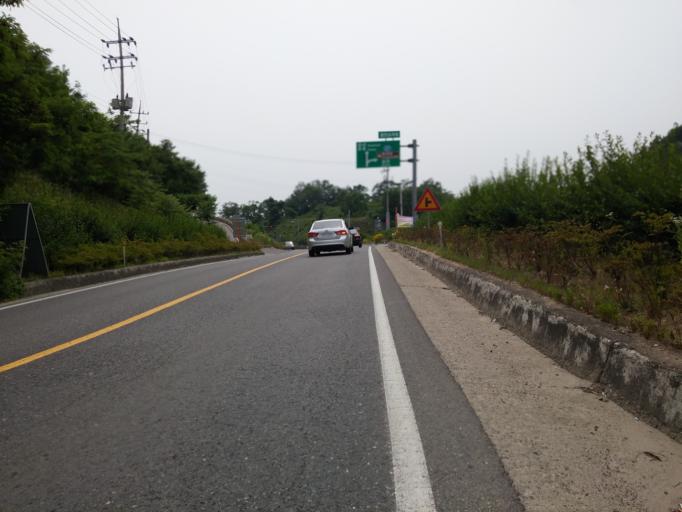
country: KR
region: Chungcheongbuk-do
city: Okcheon
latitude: 36.3063
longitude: 127.5511
